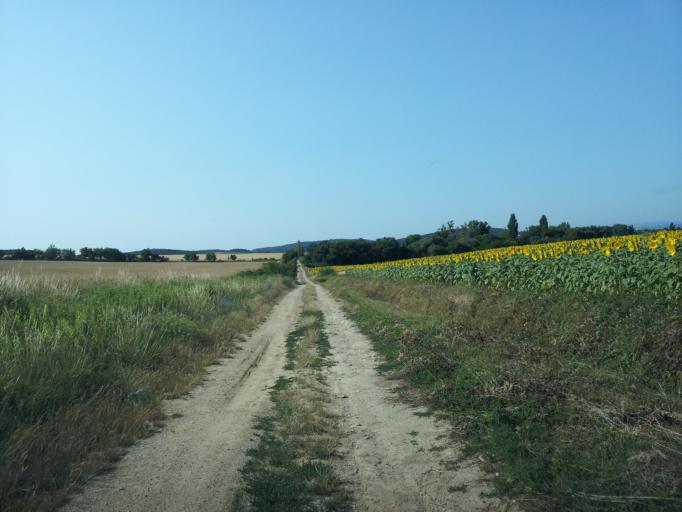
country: HU
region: Zala
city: Cserszegtomaj
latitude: 46.8497
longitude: 17.2306
